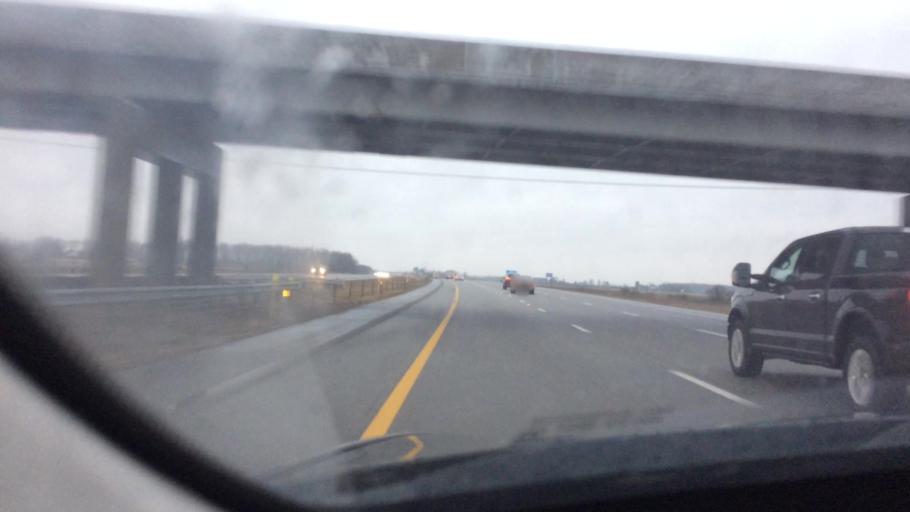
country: US
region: Ohio
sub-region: Wood County
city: Bowling Green
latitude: 41.3108
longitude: -83.6268
